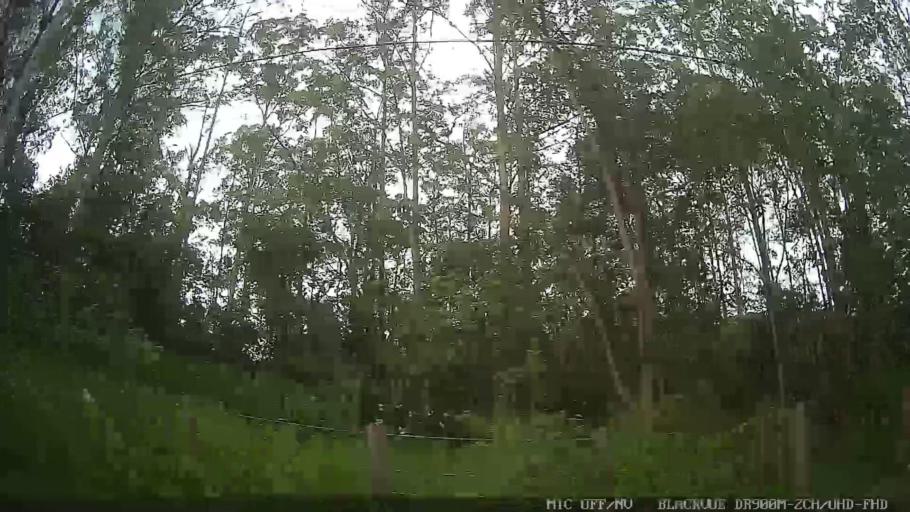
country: BR
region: Sao Paulo
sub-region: Ribeirao Pires
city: Ribeirao Pires
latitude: -23.6728
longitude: -46.3193
